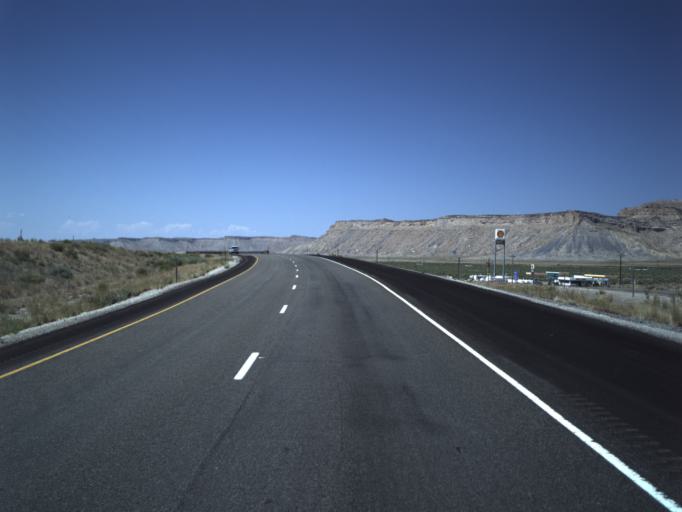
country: US
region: Utah
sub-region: Grand County
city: Moab
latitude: 38.9621
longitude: -109.7182
